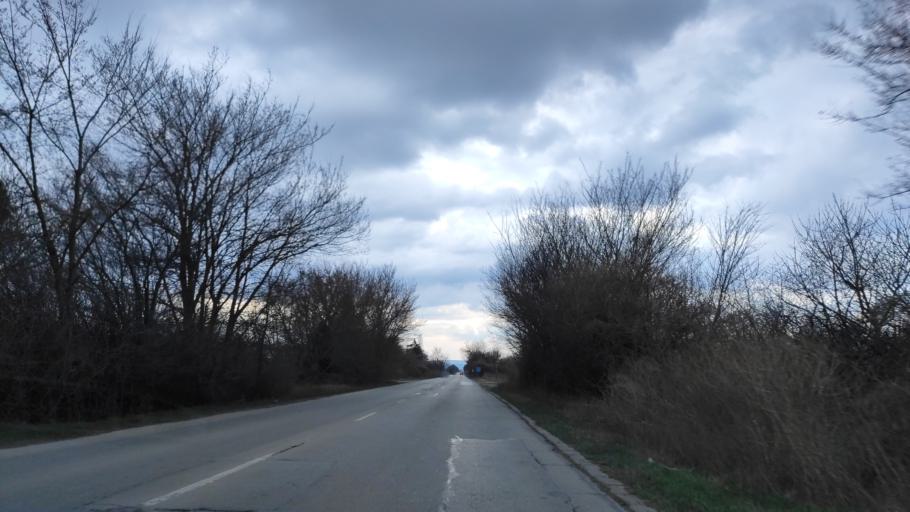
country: BG
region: Varna
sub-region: Obshtina Aksakovo
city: Aksakovo
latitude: 43.2292
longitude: 27.8287
